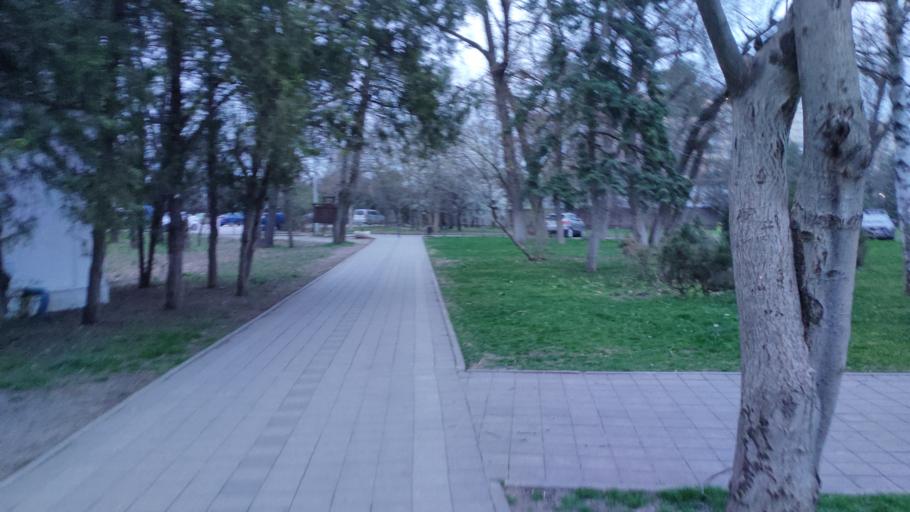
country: RU
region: Krasnodarskiy
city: Krasnodar
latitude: 45.0608
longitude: 38.9938
